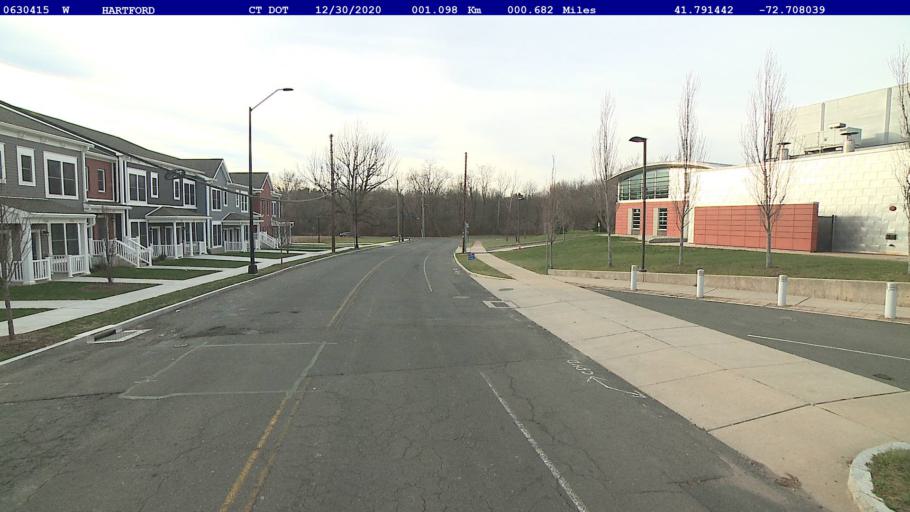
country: US
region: Connecticut
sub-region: Hartford County
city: Blue Hills
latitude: 41.7914
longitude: -72.7080
